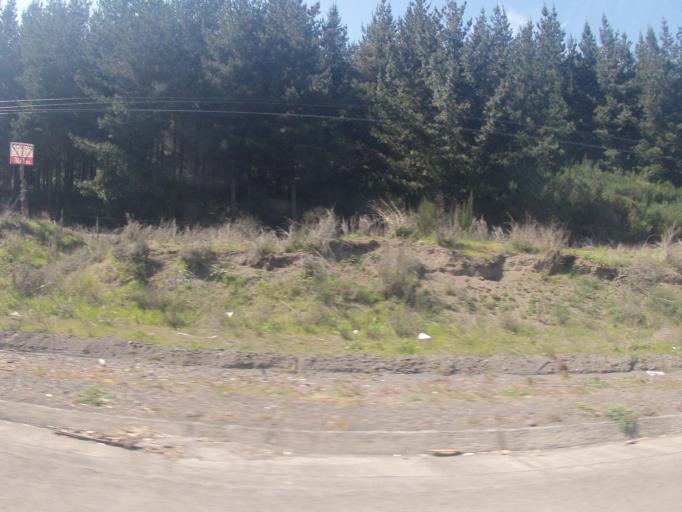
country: CL
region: Biobio
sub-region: Provincia de Biobio
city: Los Angeles
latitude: -37.3557
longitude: -72.3705
